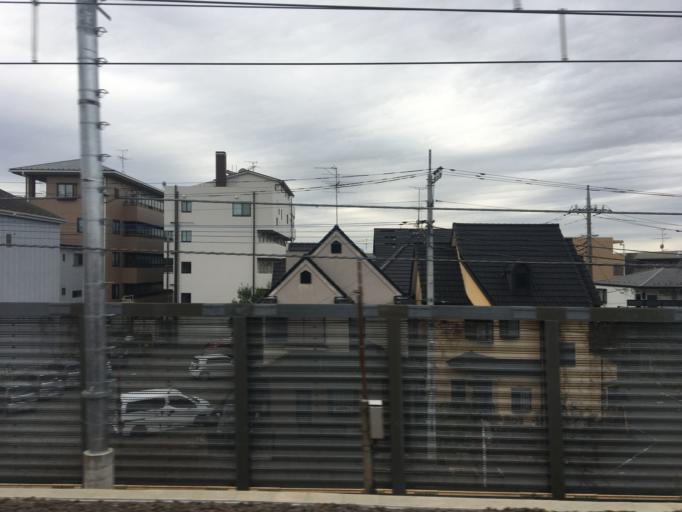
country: JP
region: Chiba
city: Nagareyama
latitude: 35.8401
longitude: 139.9020
